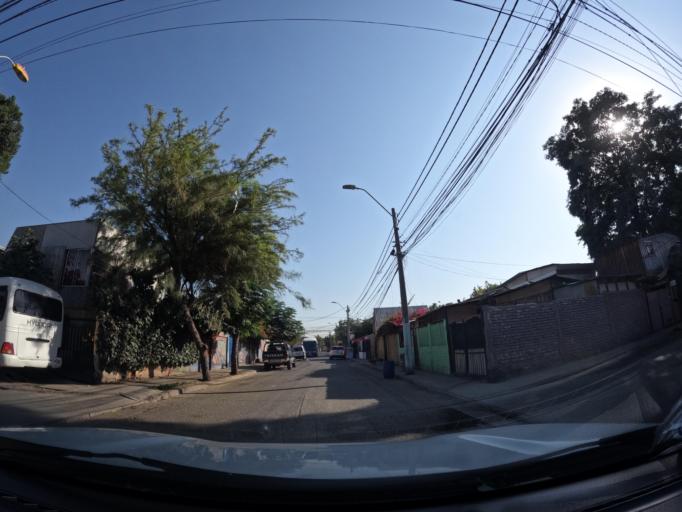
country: CL
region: Santiago Metropolitan
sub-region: Provincia de Santiago
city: Villa Presidente Frei, Nunoa, Santiago, Chile
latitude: -33.5090
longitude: -70.5658
